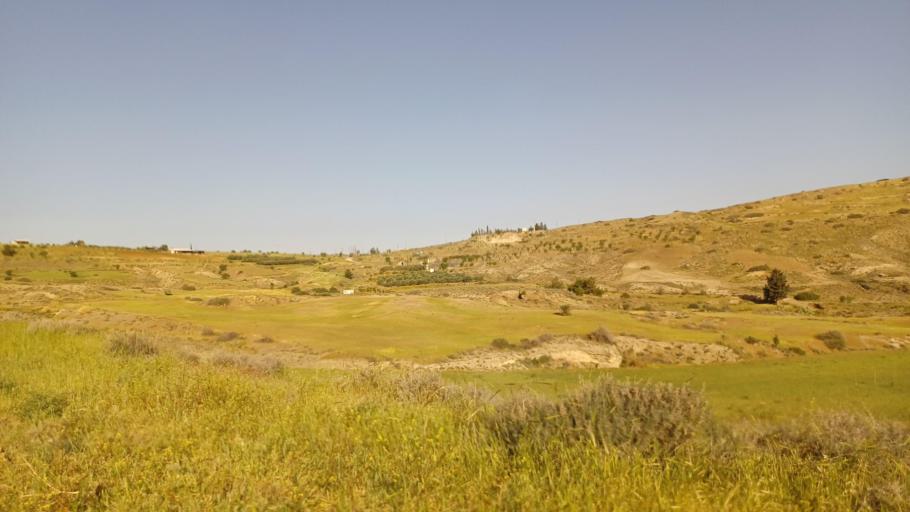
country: CY
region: Lefkosia
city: Astromeritis
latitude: 35.0768
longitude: 33.0276
